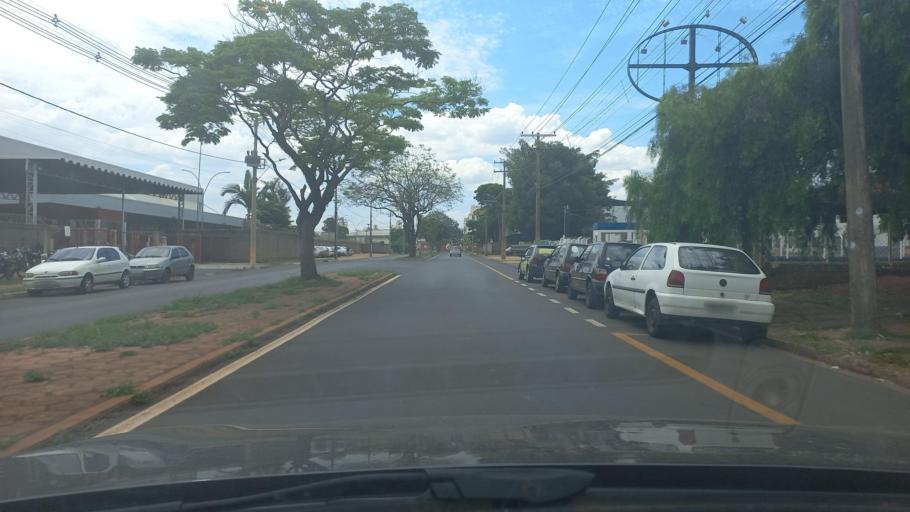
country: BR
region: Minas Gerais
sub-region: Uberaba
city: Uberaba
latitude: -19.7449
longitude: -47.9781
